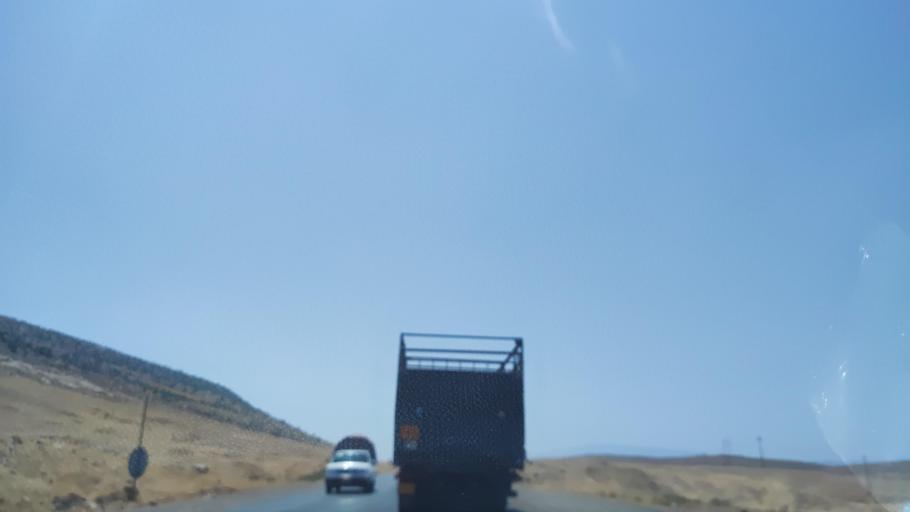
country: IQ
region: Arbil
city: Shaqlawah
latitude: 36.5937
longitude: 44.3187
